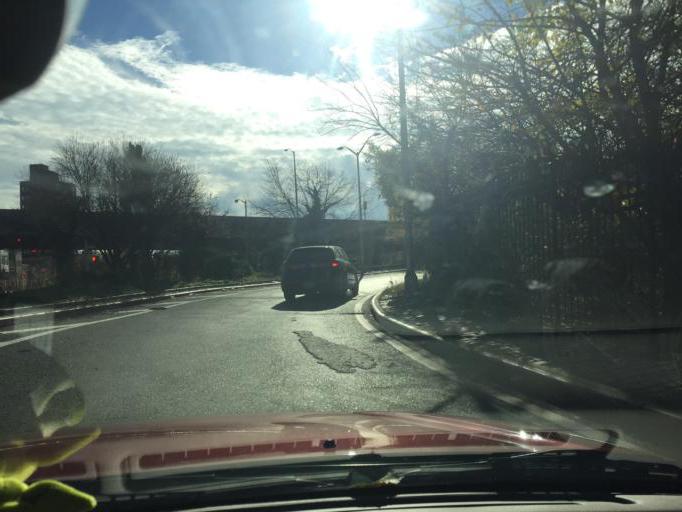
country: US
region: New York
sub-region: Queens County
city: Long Island City
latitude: 40.7207
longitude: -73.9450
